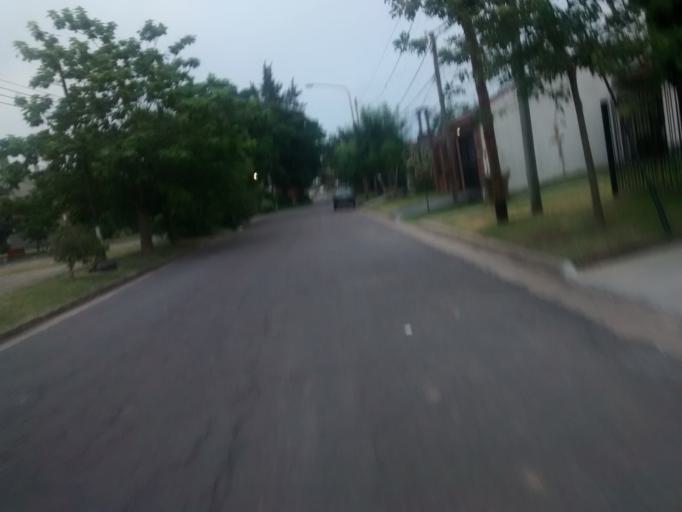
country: AR
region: Buenos Aires
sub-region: Partido de La Plata
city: La Plata
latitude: -34.9443
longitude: -57.9213
